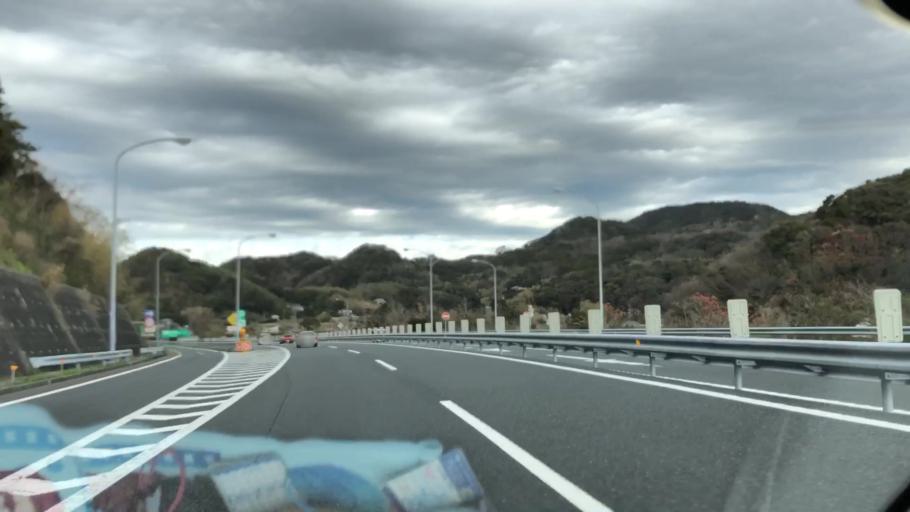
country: JP
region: Chiba
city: Tateyama
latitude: 35.0974
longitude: 139.8596
